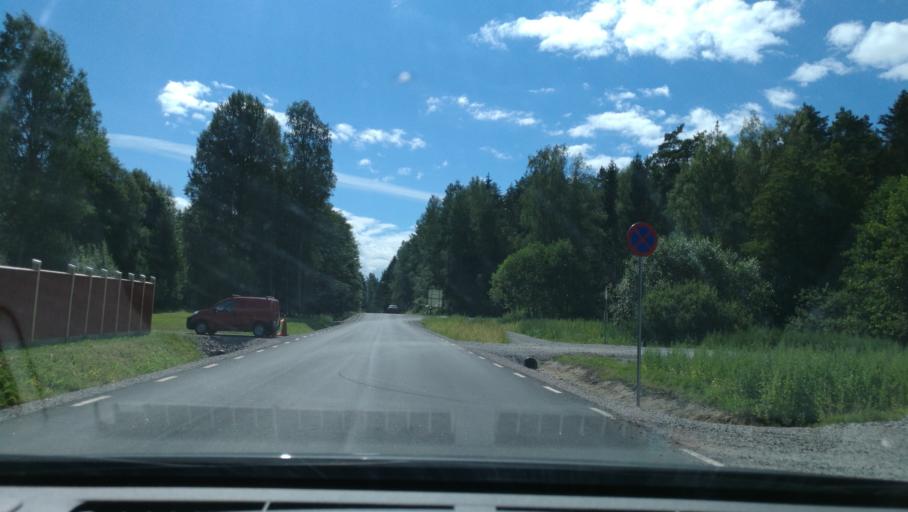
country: SE
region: OEstergoetland
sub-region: Norrkopings Kommun
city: Krokek
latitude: 58.6655
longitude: 16.4682
